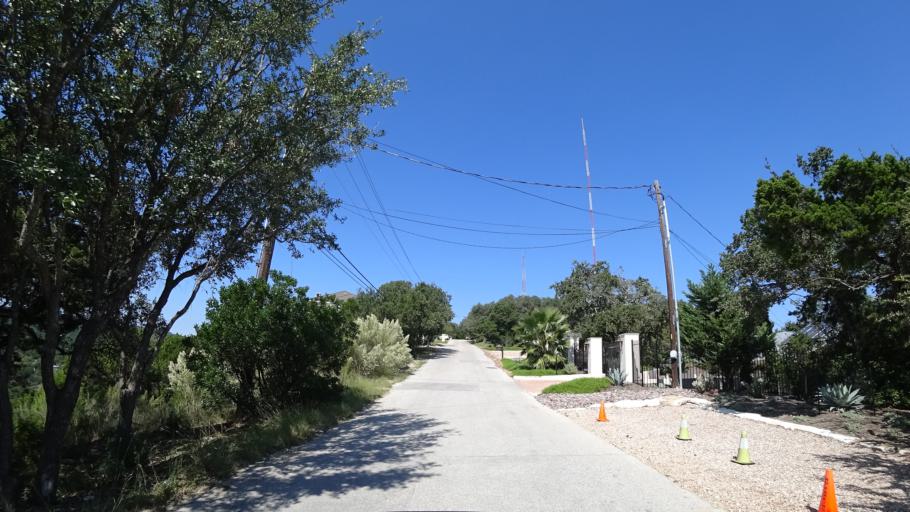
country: US
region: Texas
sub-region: Travis County
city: West Lake Hills
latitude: 30.3057
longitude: -97.7925
